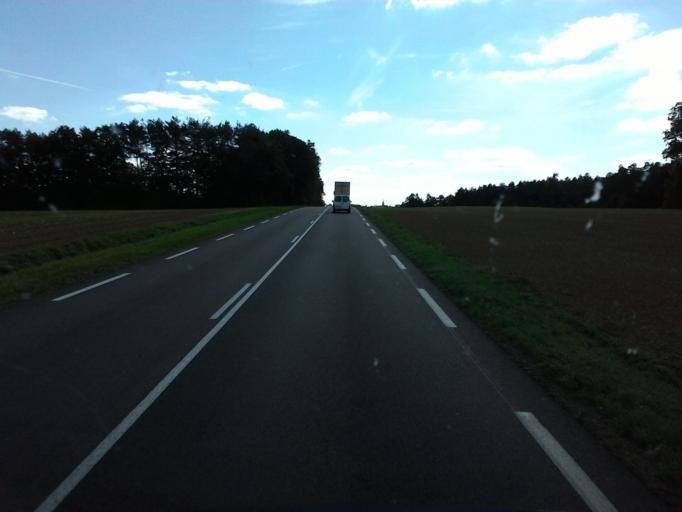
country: FR
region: Bourgogne
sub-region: Departement de la Cote-d'Or
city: Chatillon-sur-Seine
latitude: 47.7717
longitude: 4.5051
